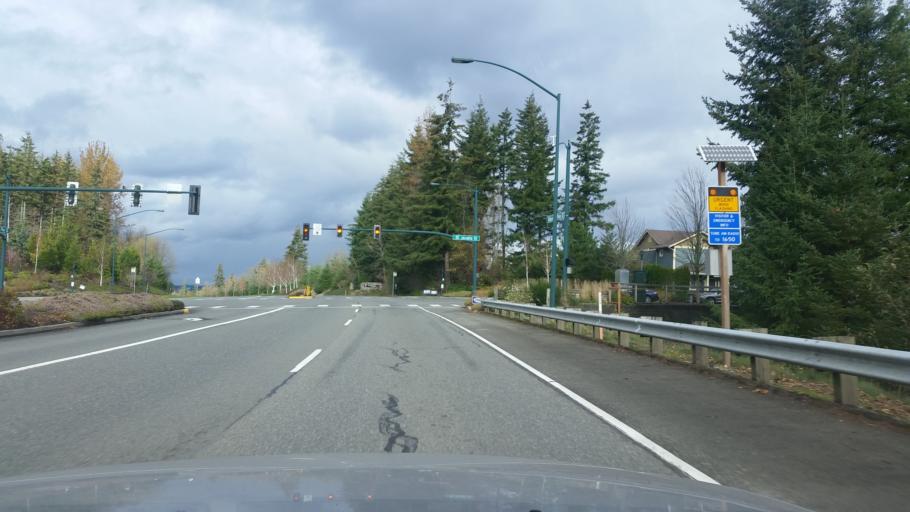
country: US
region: Washington
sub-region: King County
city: Fall City
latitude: 47.5159
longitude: -121.8798
